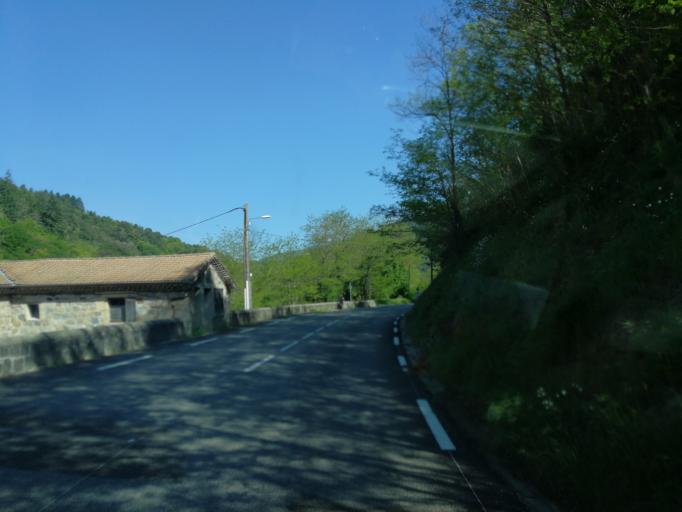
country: FR
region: Rhone-Alpes
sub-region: Departement de l'Ardeche
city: Saint-Sauveur-de-Montagut
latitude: 44.8455
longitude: 4.5722
